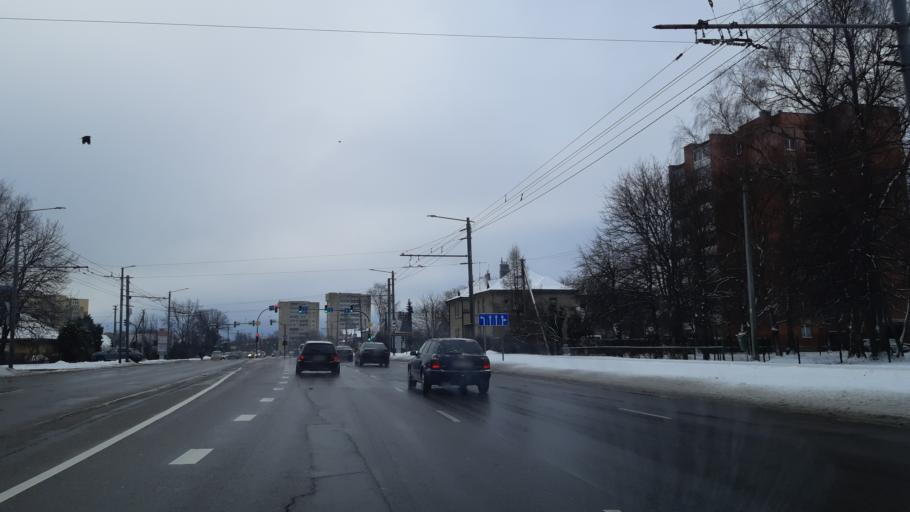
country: LT
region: Kauno apskritis
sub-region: Kaunas
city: Eiguliai
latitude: 54.9113
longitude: 23.9402
